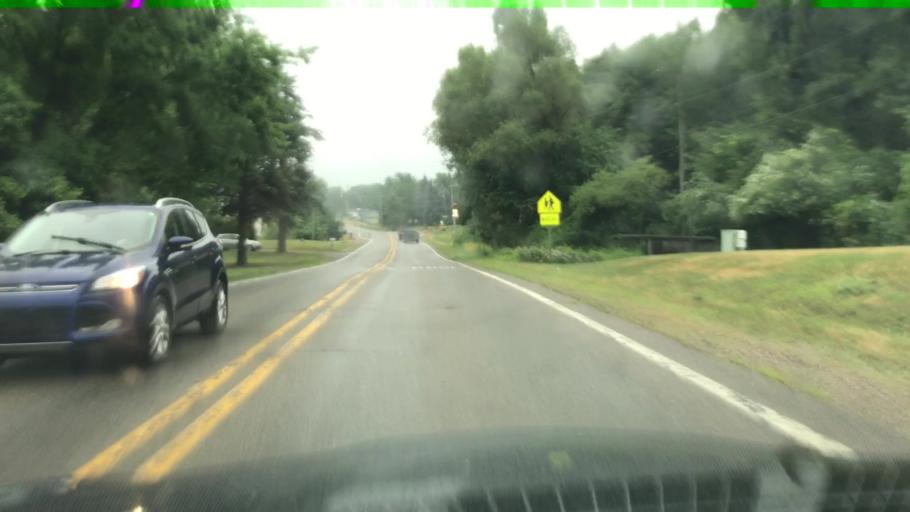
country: US
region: Michigan
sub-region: Oakland County
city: Auburn Hills
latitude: 42.7314
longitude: -83.2880
